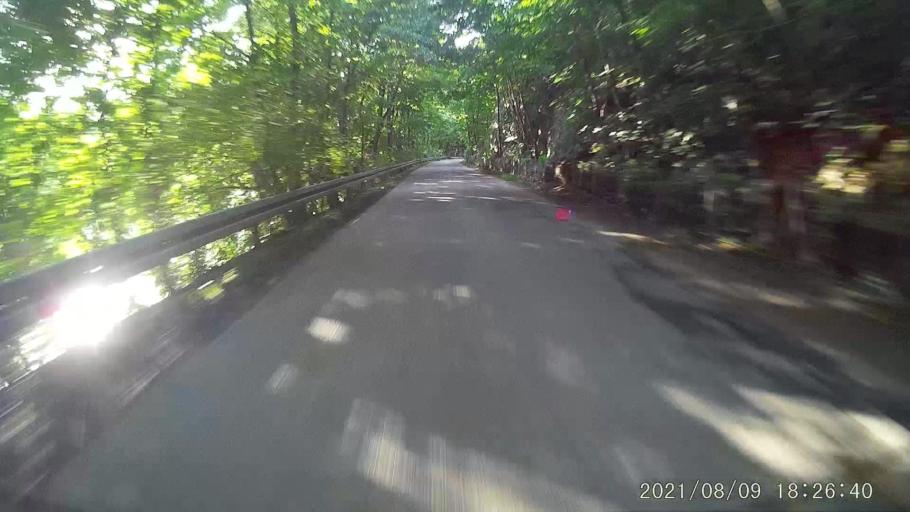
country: PL
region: Lower Silesian Voivodeship
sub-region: Powiat zabkowicki
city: Bardo
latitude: 50.5095
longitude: 16.7360
